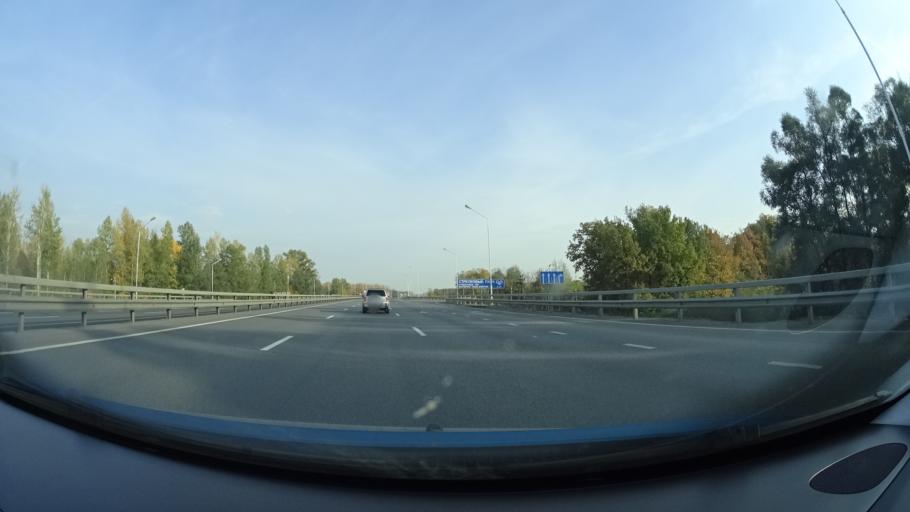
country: RU
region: Bashkortostan
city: Ufa
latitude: 54.6587
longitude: 55.8877
